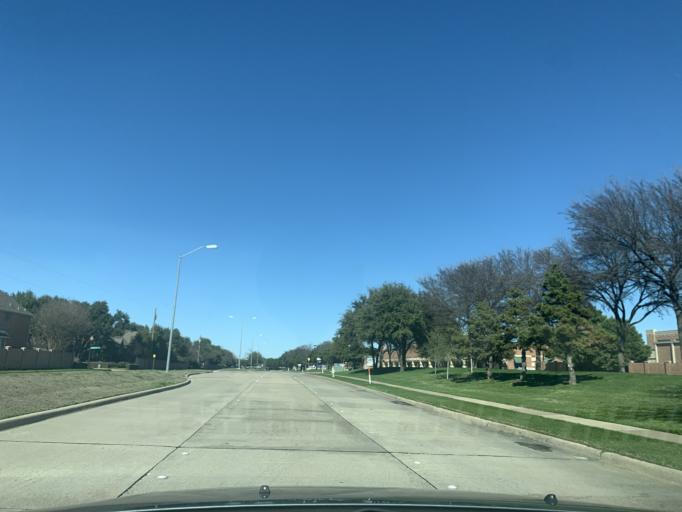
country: US
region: Texas
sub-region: Denton County
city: The Colony
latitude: 33.0473
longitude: -96.8330
